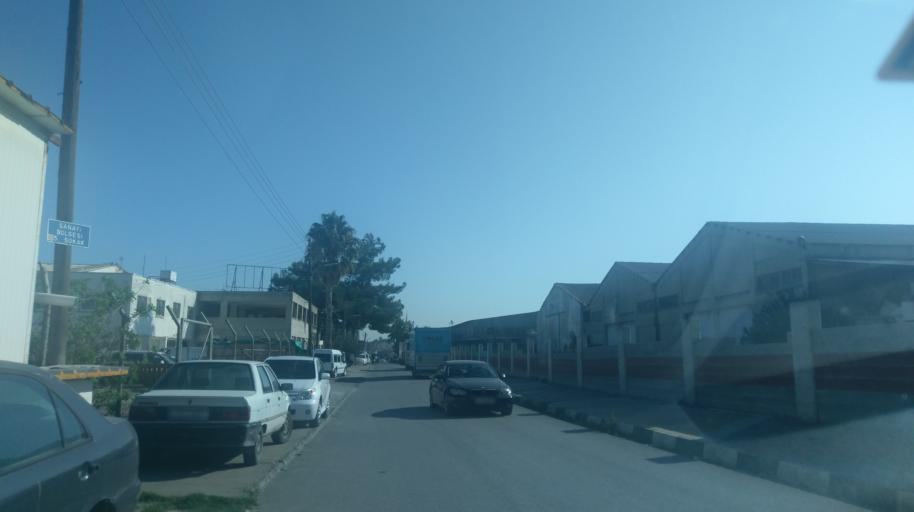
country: CY
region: Lefkosia
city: Nicosia
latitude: 35.2149
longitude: 33.3405
